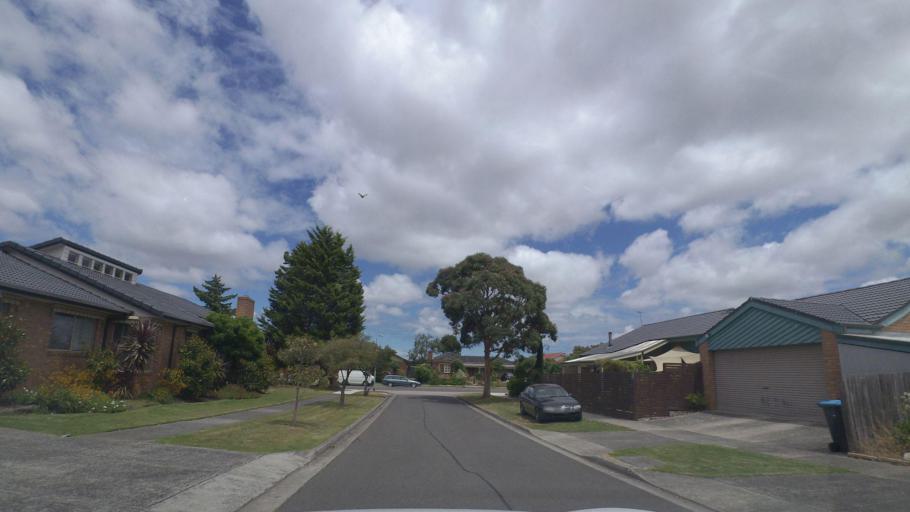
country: AU
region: Victoria
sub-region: Knox
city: Knoxfield
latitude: -37.9080
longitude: 145.2633
